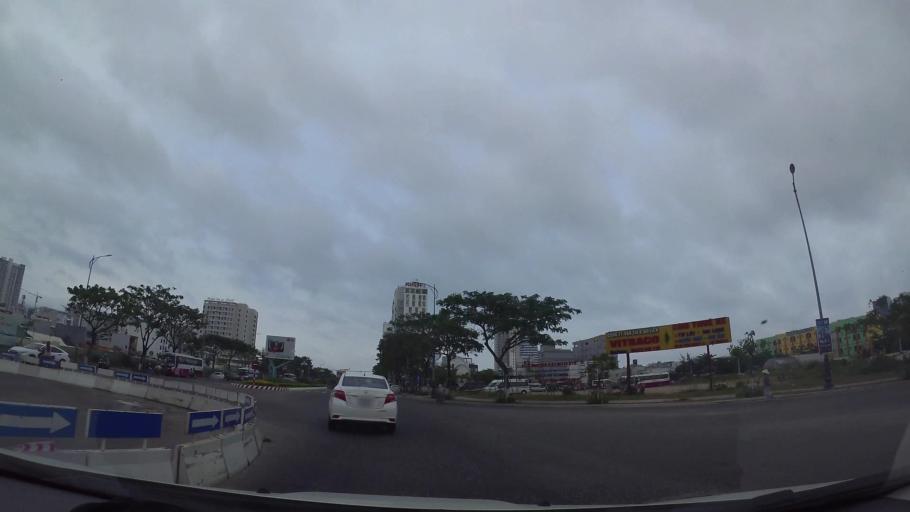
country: VN
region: Da Nang
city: Son Tra
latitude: 16.0623
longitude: 108.2401
